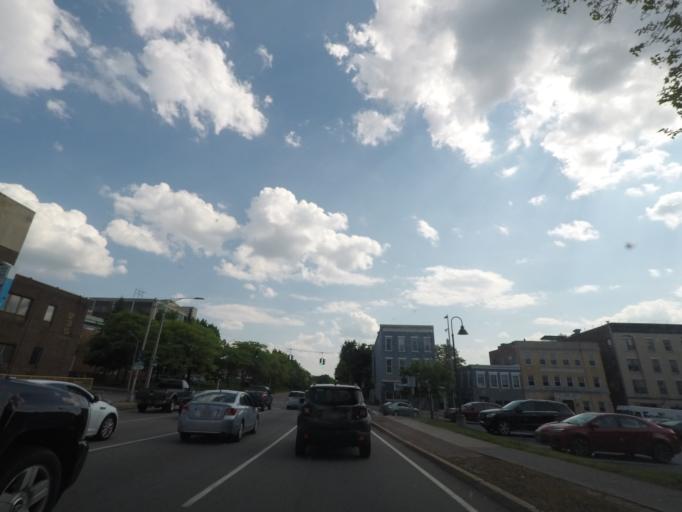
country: US
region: New York
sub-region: Dutchess County
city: Poughkeepsie
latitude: 41.7050
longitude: -73.9301
